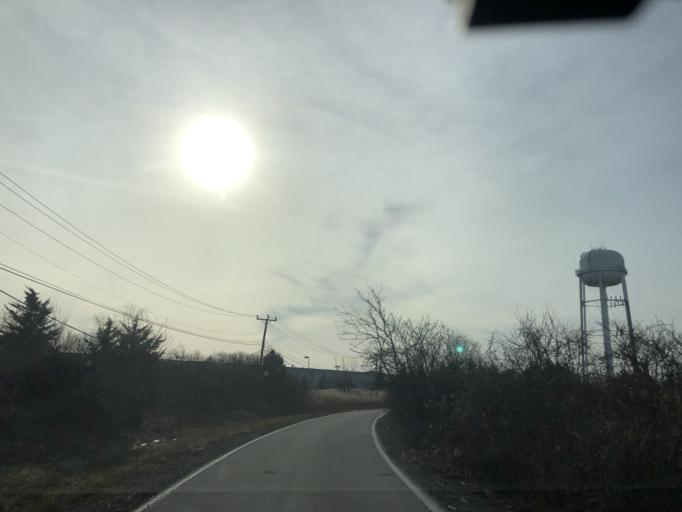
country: US
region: Illinois
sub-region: Cook County
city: Lemont
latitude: 41.7026
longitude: -88.0269
